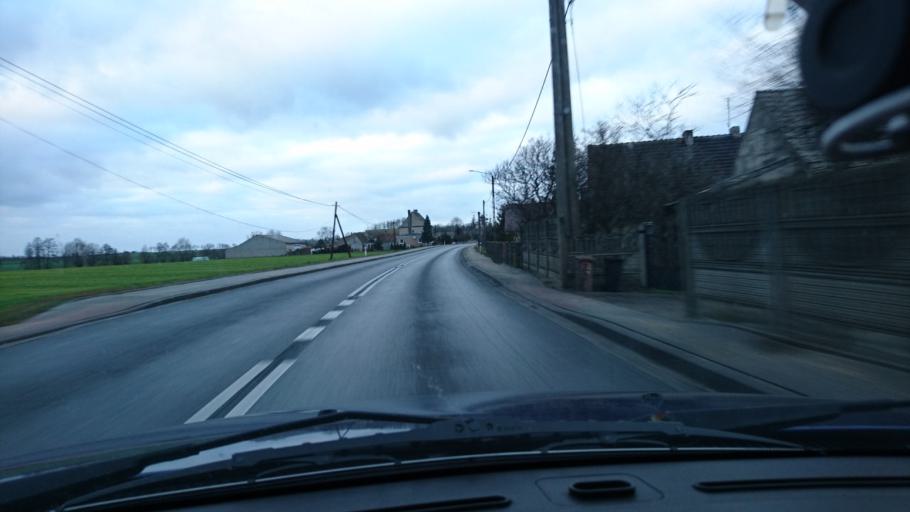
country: PL
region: Greater Poland Voivodeship
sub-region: Powiat kepinski
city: Opatow
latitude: 51.1671
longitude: 18.1470
